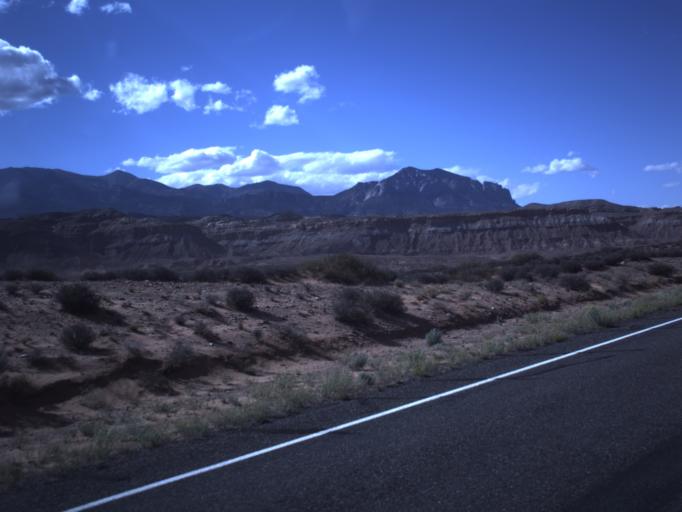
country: US
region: Utah
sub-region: Wayne County
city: Loa
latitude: 38.0776
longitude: -110.6106
